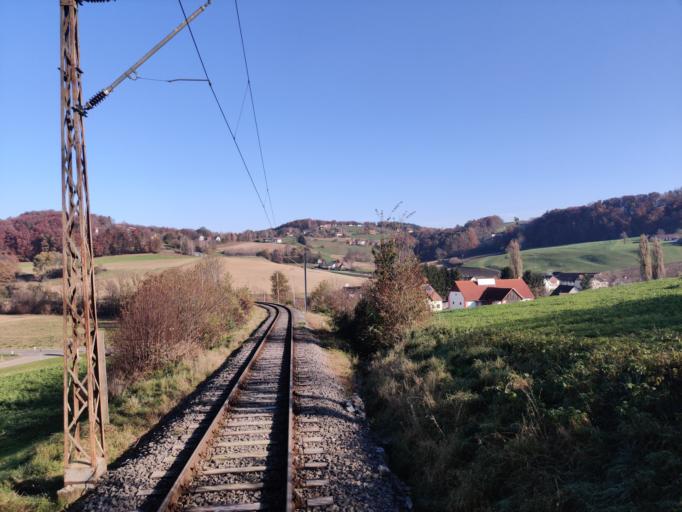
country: AT
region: Styria
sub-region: Politischer Bezirk Suedoststeiermark
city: Maierdorf
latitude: 46.8801
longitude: 15.8487
